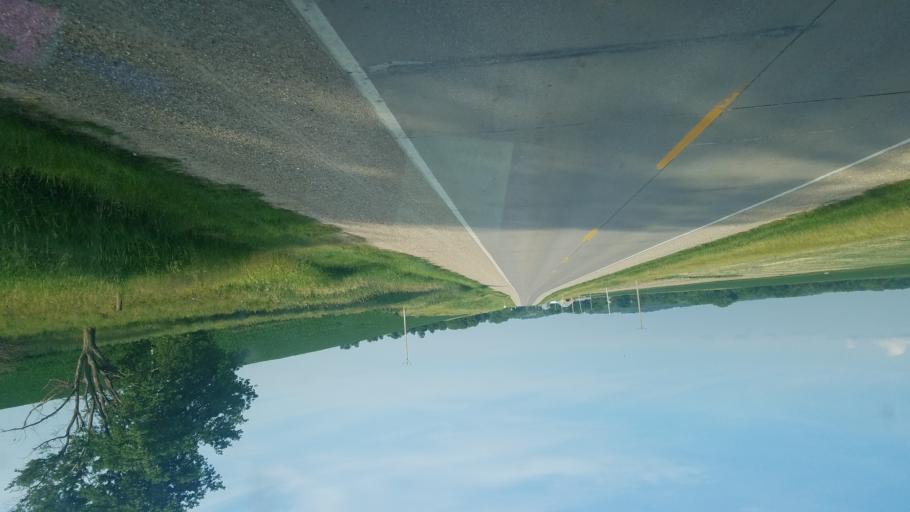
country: US
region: Iowa
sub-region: Tama County
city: Toledo
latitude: 41.9895
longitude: -92.7233
